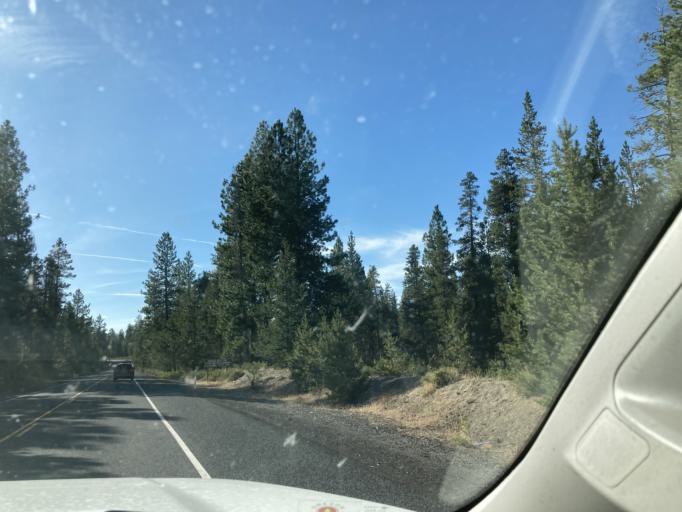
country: US
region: Oregon
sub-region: Deschutes County
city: Three Rivers
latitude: 43.8162
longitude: -121.4942
